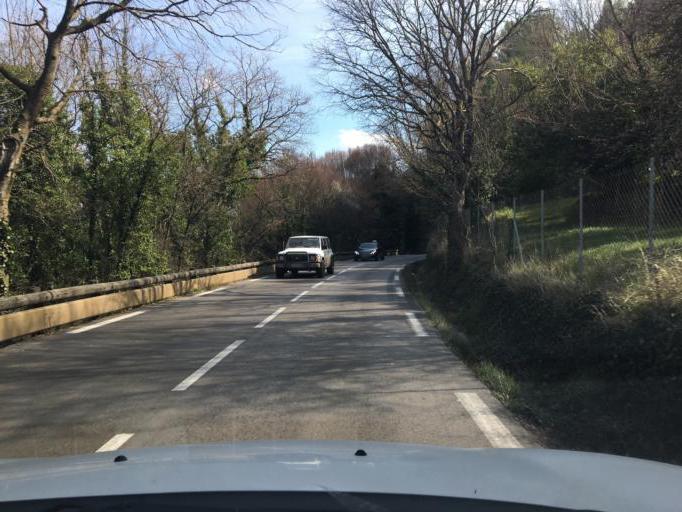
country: FR
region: Provence-Alpes-Cote d'Azur
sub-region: Departement du Var
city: Flayosc
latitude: 43.5368
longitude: 6.3994
